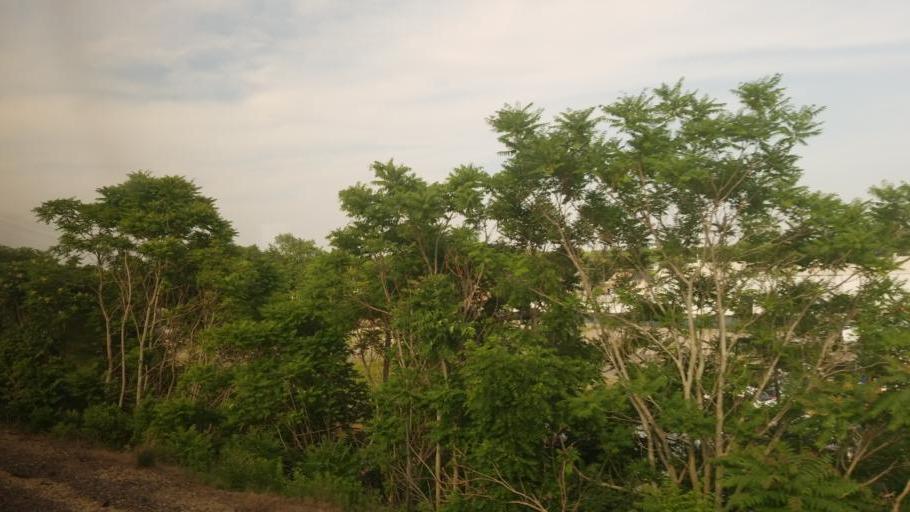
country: US
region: Illinois
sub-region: Kane County
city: Montgomery
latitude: 41.7442
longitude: -88.3338
